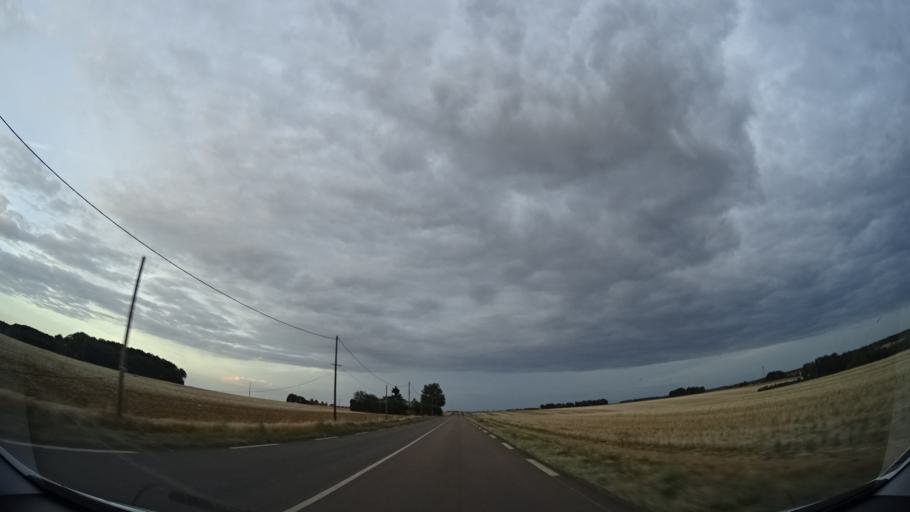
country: FR
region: Bourgogne
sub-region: Departement de l'Yonne
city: Charny
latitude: 47.9322
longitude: 3.1706
